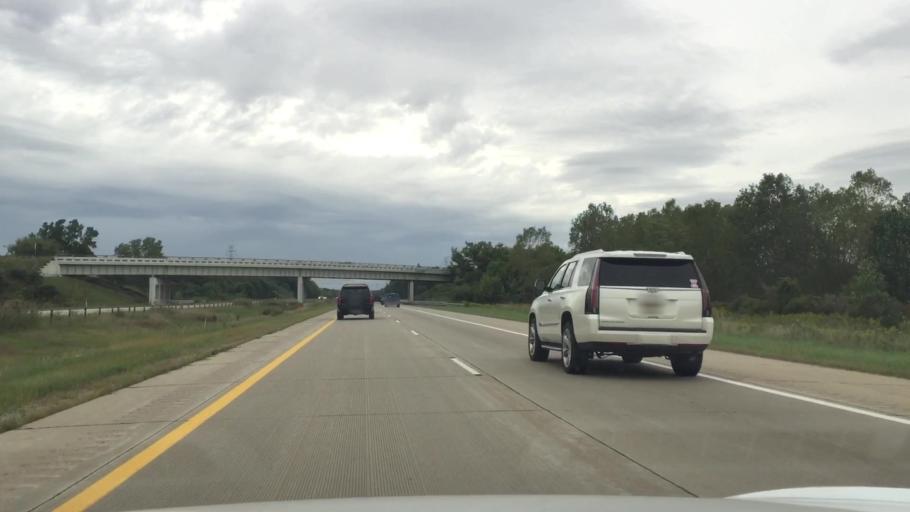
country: US
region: Michigan
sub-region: Macomb County
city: Richmond
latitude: 42.7525
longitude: -82.7076
